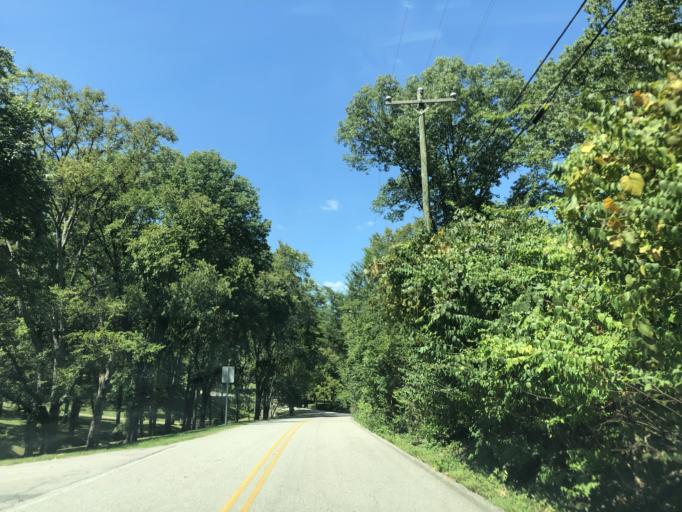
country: US
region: Tennessee
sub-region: Davidson County
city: Oak Hill
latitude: 36.0764
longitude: -86.7905
